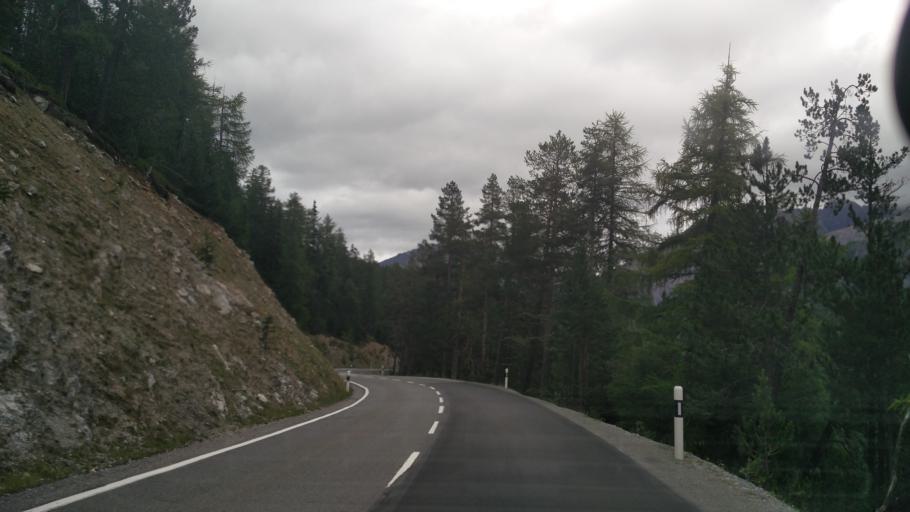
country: CH
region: Grisons
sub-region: Inn District
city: Zernez
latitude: 46.6767
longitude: 10.1653
